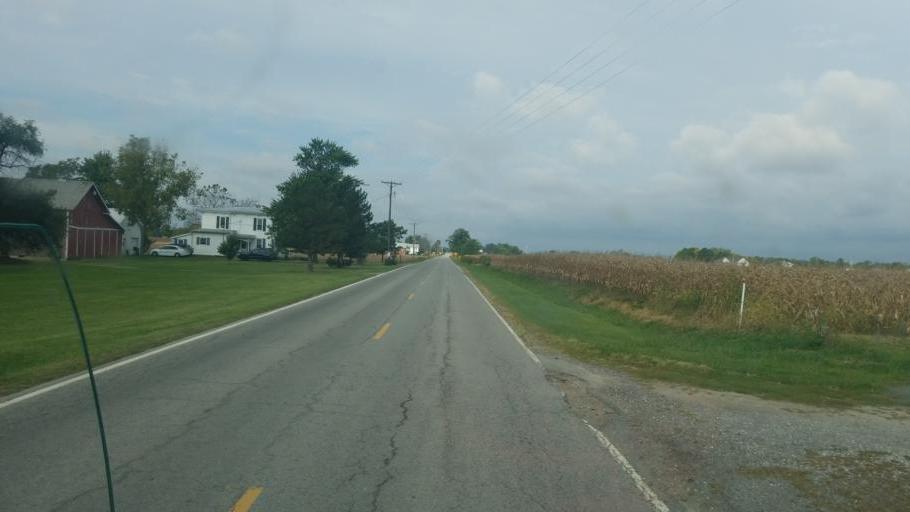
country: US
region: Ohio
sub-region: Wyandot County
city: Carey
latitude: 41.0355
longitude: -83.4725
